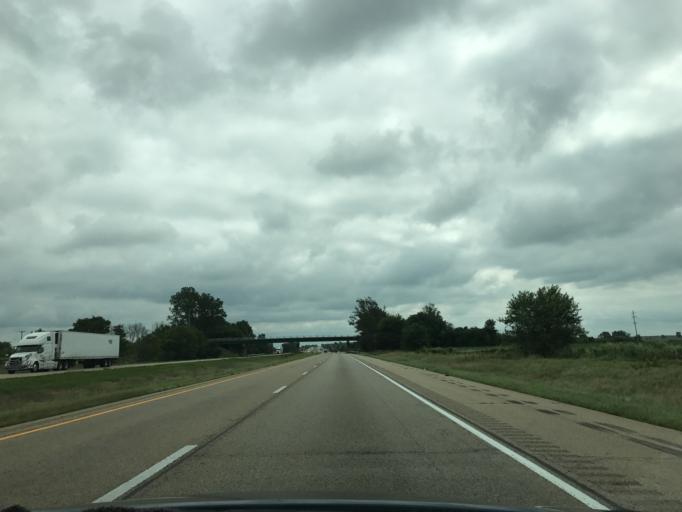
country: US
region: Illinois
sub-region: Henry County
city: Kewanee
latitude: 41.3863
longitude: -89.7694
